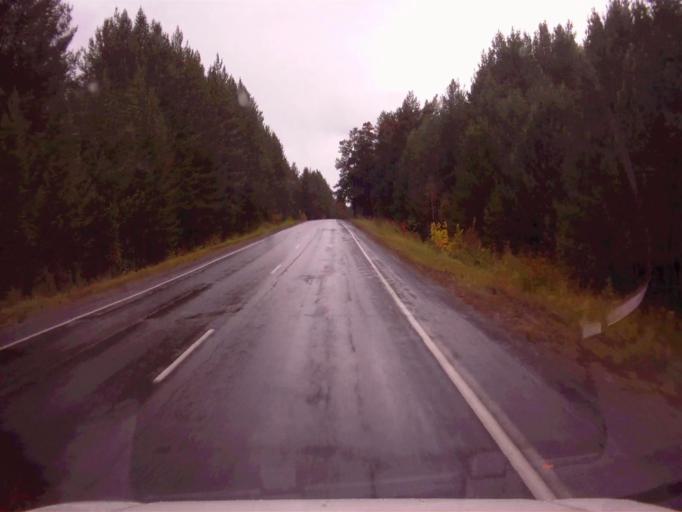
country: RU
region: Chelyabinsk
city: Verkhniy Ufaley
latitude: 56.0204
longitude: 60.3031
